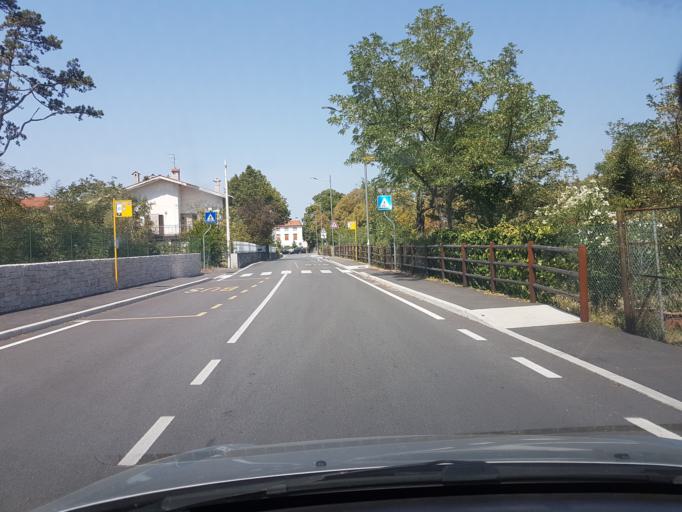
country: IT
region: Friuli Venezia Giulia
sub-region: Provincia di Trieste
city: Aurisina
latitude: 45.7516
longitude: 13.6884
